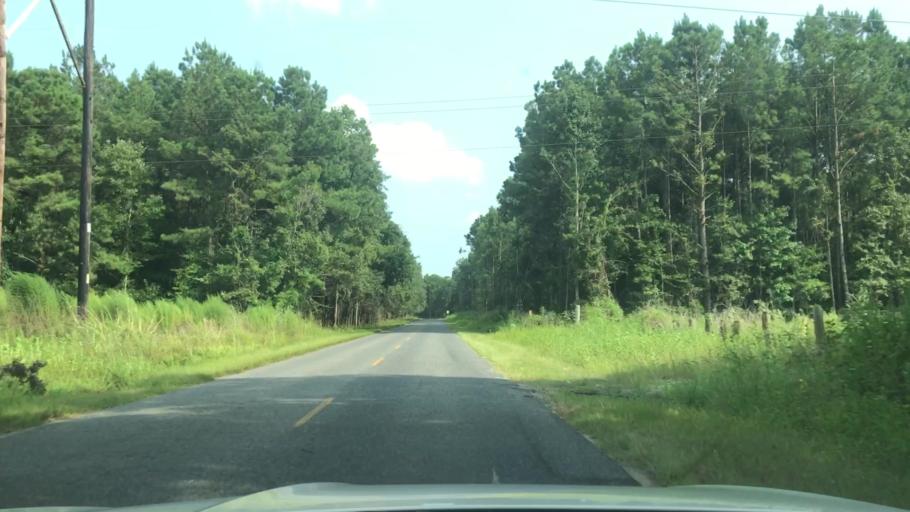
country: US
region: South Carolina
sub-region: Charleston County
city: Shell Point
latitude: 32.8182
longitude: -80.0914
